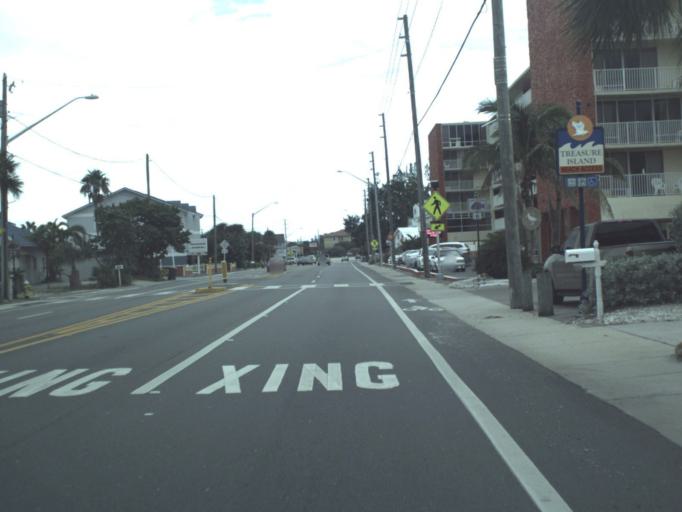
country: US
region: Florida
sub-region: Pinellas County
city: Treasure Island
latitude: 27.7596
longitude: -82.7658
